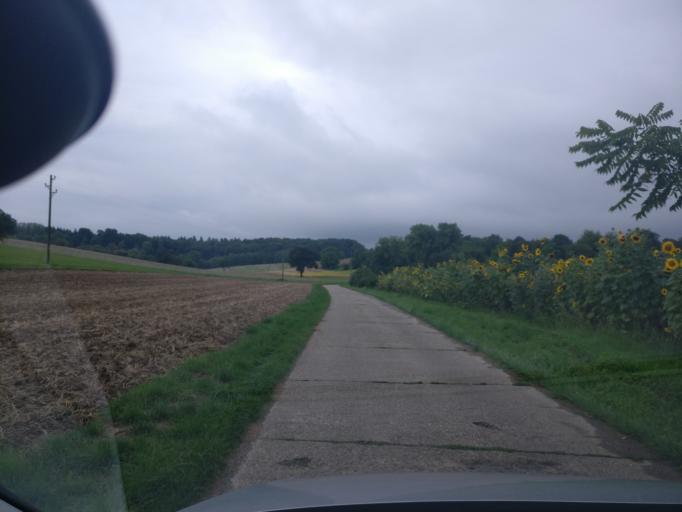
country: DE
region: Baden-Wuerttemberg
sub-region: Karlsruhe Region
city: Woessingen
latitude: 49.0068
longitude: 8.5941
